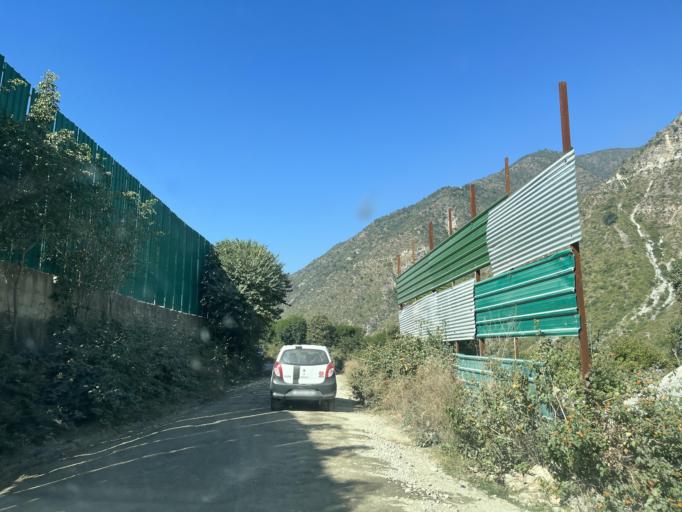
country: IN
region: Uttarakhand
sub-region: Almora
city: Ranikhet
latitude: 29.5525
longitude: 79.3984
